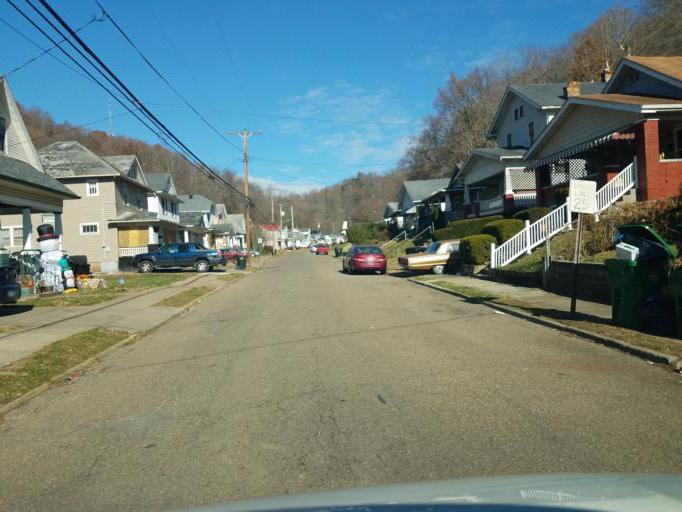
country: US
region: Kentucky
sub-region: Greenup County
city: South Shore
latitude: 38.7461
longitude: -82.9651
